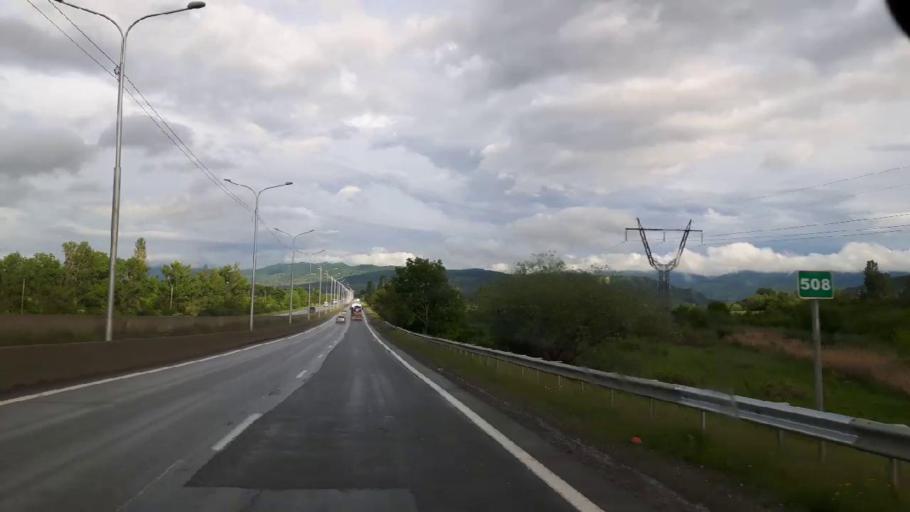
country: GE
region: Shida Kartli
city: Kaspi
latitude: 41.9253
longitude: 44.5382
